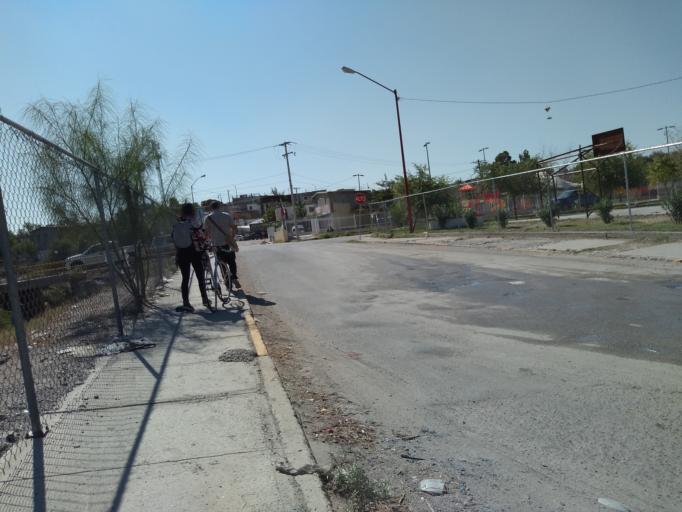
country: US
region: Texas
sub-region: El Paso County
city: El Paso
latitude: 31.7573
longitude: -106.5037
